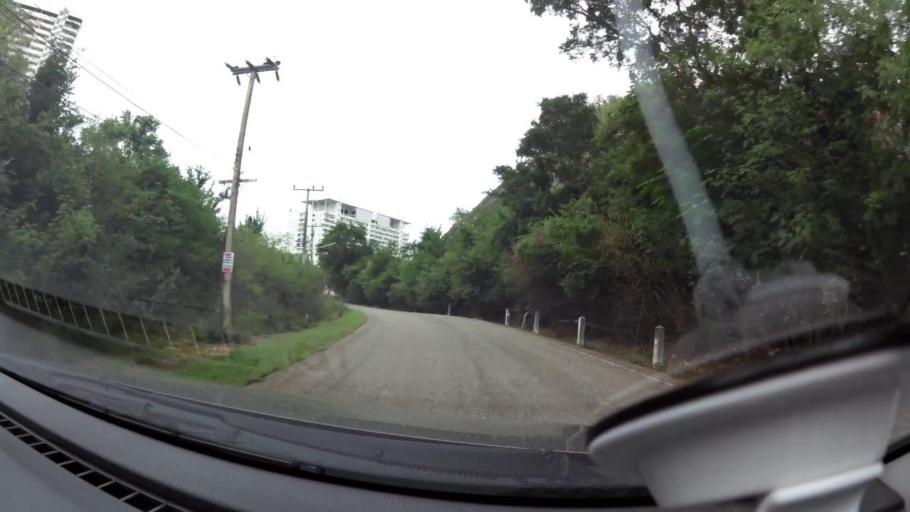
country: TH
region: Prachuap Khiri Khan
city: Pran Buri
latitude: 12.4328
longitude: 99.9777
